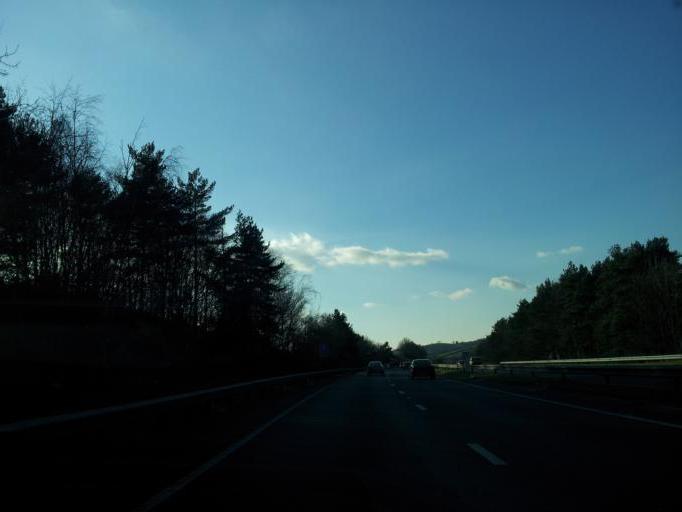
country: GB
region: England
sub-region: Devon
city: Exeter
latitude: 50.7196
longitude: -3.5963
